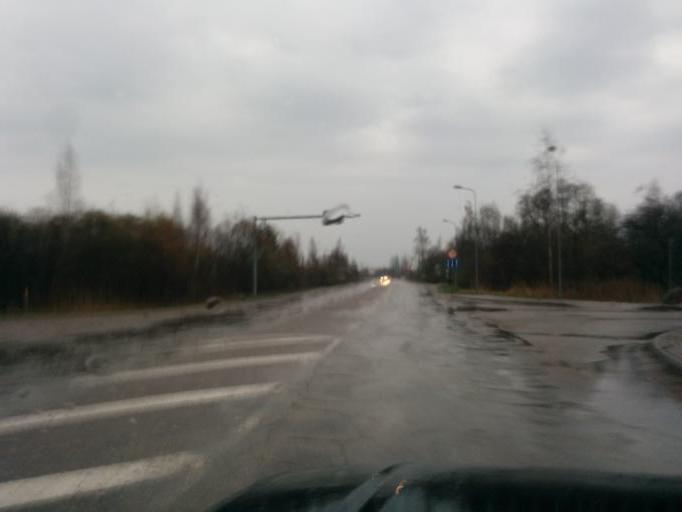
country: LV
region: Ozolnieku
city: Ozolnieki
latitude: 56.6584
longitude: 23.7899
